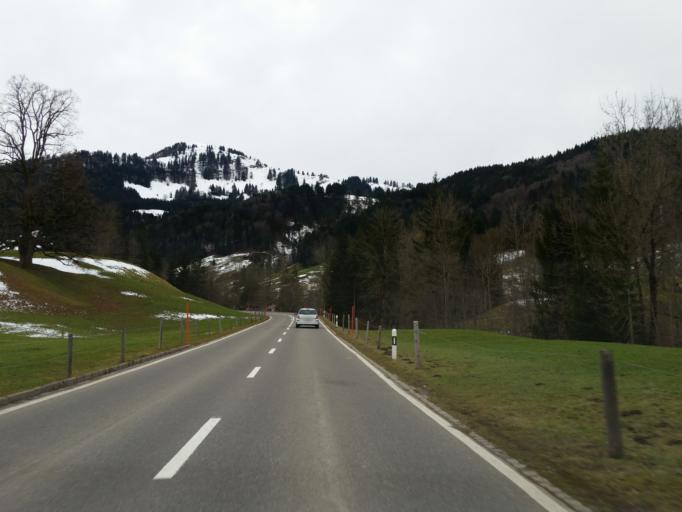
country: CH
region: Appenzell Ausserrhoden
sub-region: Bezirk Hinterland
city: Urnasch
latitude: 47.2992
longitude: 9.2724
